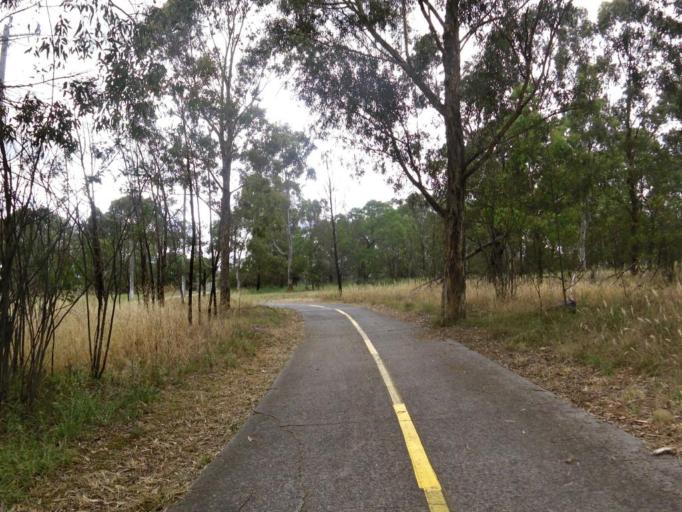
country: AU
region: Victoria
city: Heidelberg West
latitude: -37.7450
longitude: 145.0349
